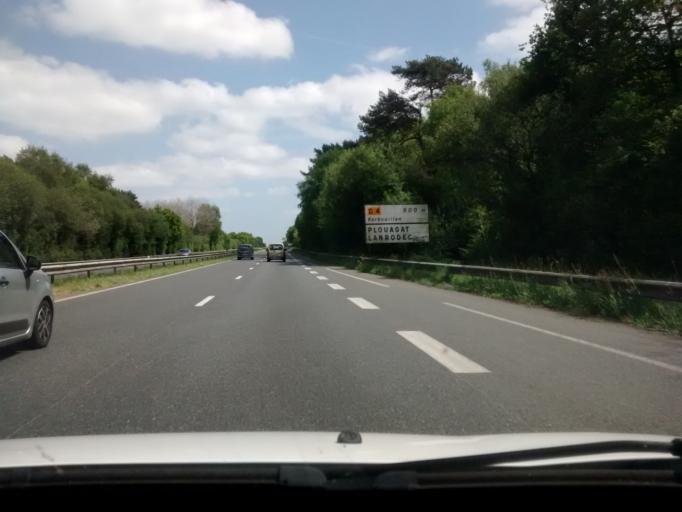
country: FR
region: Brittany
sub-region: Departement des Cotes-d'Armor
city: Plouagat
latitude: 48.5356
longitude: -3.0186
